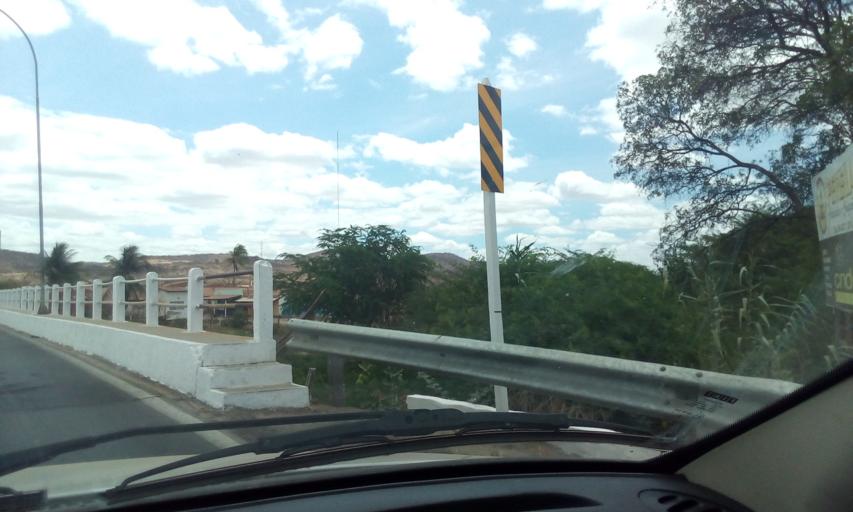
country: BR
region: Rio Grande do Norte
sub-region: Currais Novos
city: Currais Novos
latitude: -6.2573
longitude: -36.5111
